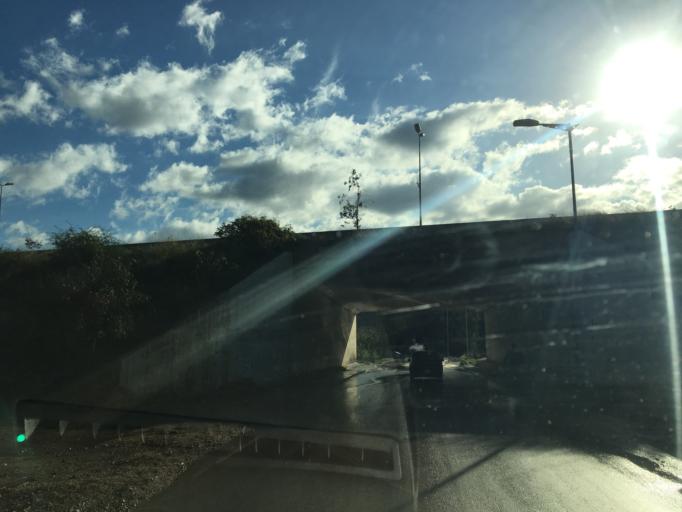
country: DZ
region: Tipaza
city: Hadjout
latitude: 36.5664
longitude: 2.3950
